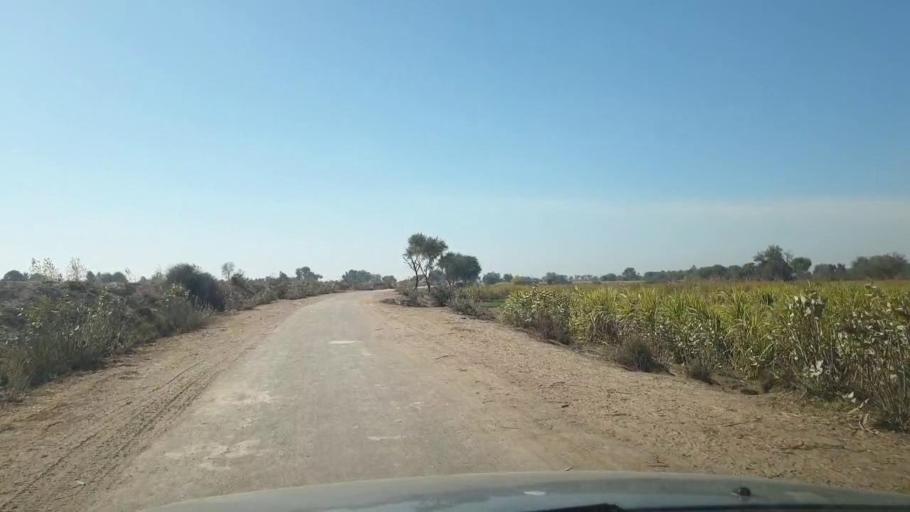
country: PK
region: Sindh
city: Ghotki
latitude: 28.0171
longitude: 69.2667
